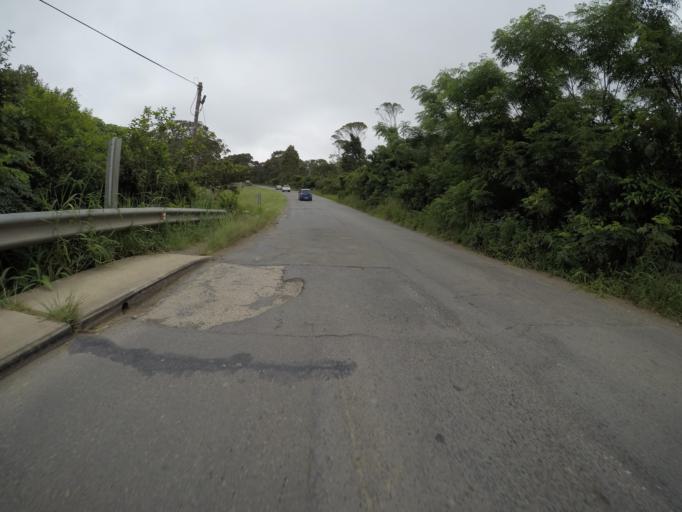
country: ZA
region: Eastern Cape
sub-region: Buffalo City Metropolitan Municipality
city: East London
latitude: -32.9386
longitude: 27.9408
